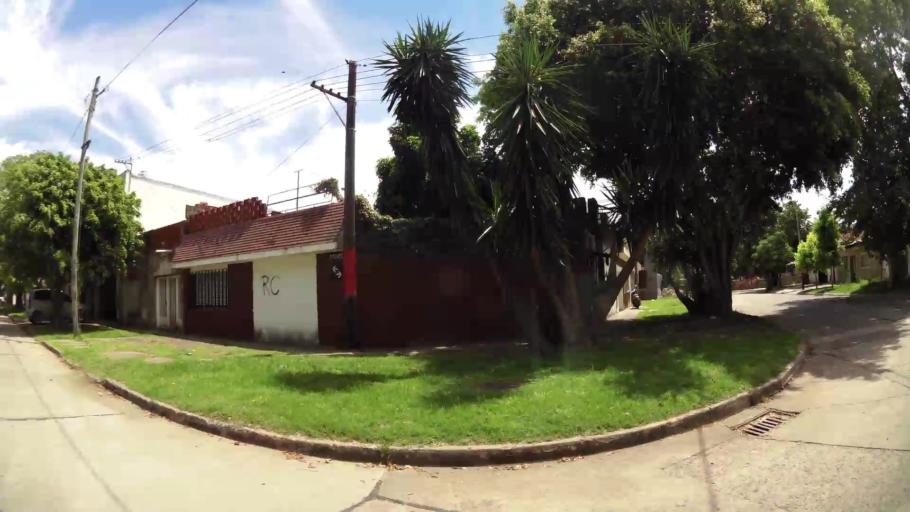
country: AR
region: Santa Fe
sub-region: Departamento de Rosario
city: Rosario
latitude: -32.9720
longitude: -60.6258
